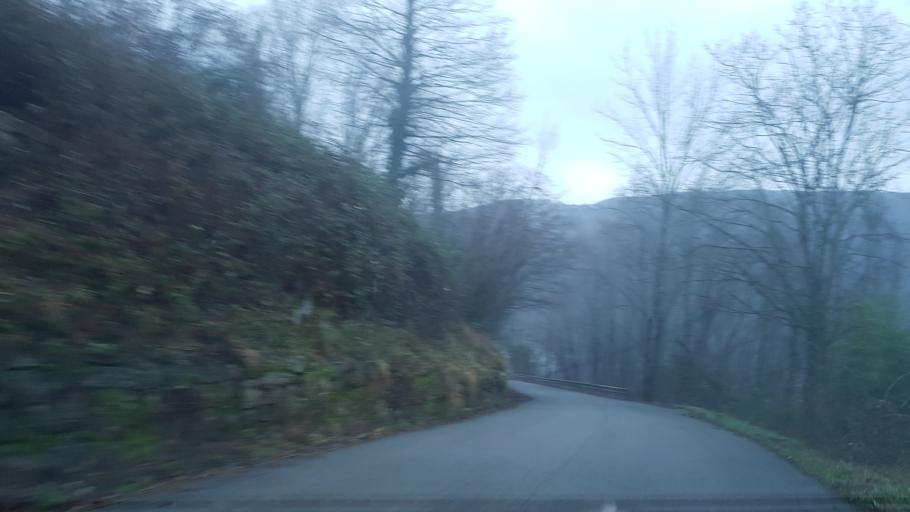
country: IT
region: Friuli Venezia Giulia
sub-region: Provincia di Udine
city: San Leonardo
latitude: 46.0884
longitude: 13.5498
